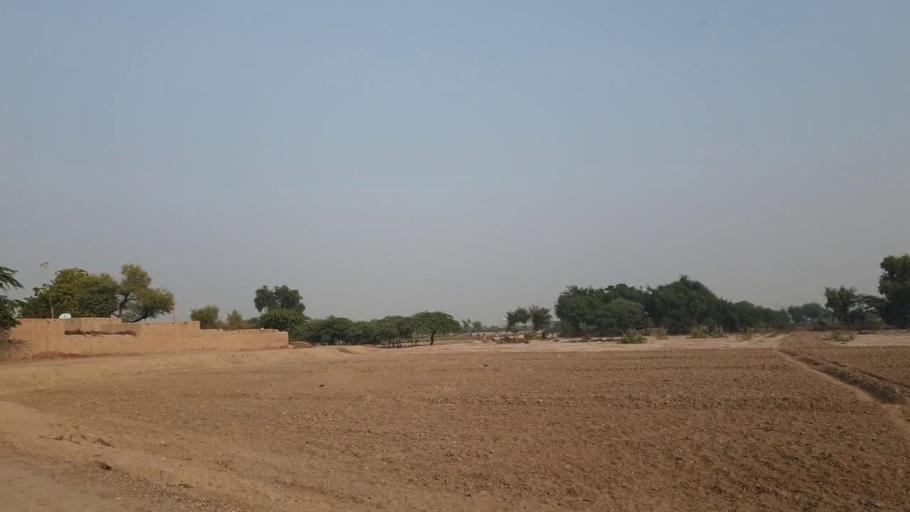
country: PK
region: Sindh
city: Bhan
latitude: 26.5589
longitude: 67.7035
